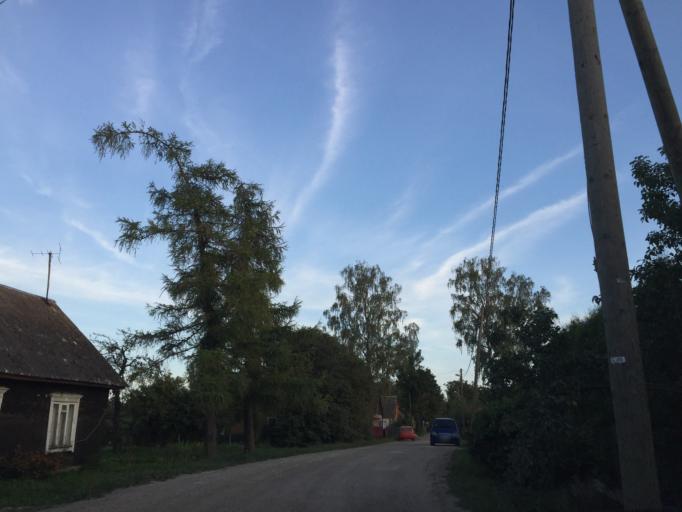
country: LV
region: Rezekne
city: Rezekne
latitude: 56.4975
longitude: 27.3463
